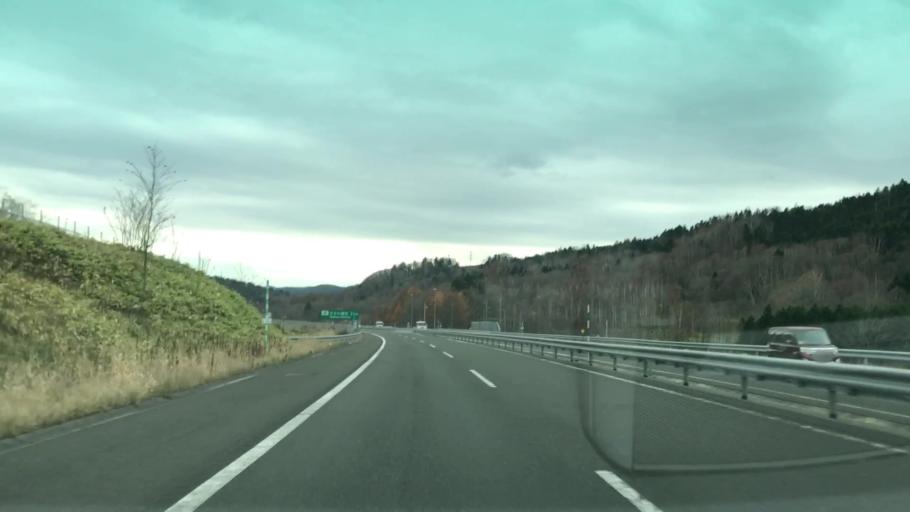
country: JP
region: Hokkaido
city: Shimo-furano
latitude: 42.9365
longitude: 142.2079
